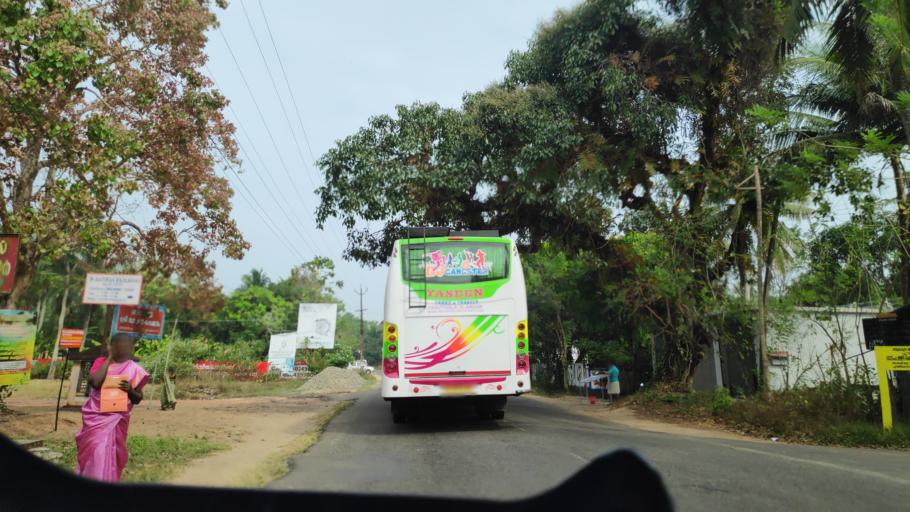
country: IN
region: Kerala
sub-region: Alappuzha
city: Kutiatodu
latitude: 9.8188
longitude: 76.3508
